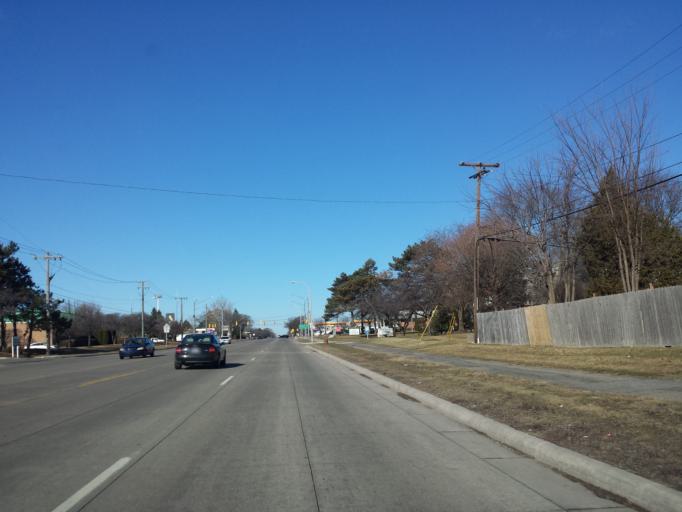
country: US
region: Michigan
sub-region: Oakland County
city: Lathrup Village
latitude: 42.5021
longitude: -83.2393
